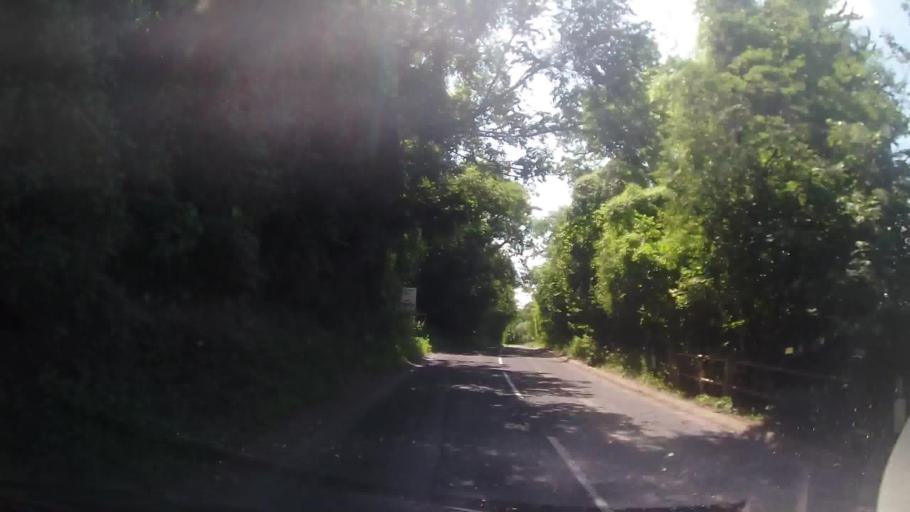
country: GB
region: England
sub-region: Herefordshire
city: Brockhampton
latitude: 52.0266
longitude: -2.6286
